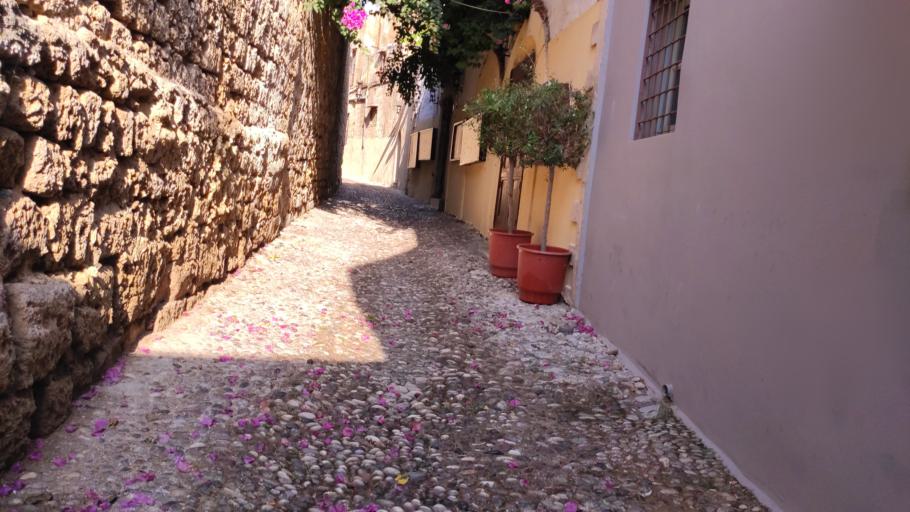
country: GR
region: South Aegean
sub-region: Nomos Dodekanisou
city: Rodos
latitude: 36.4430
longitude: 28.2245
